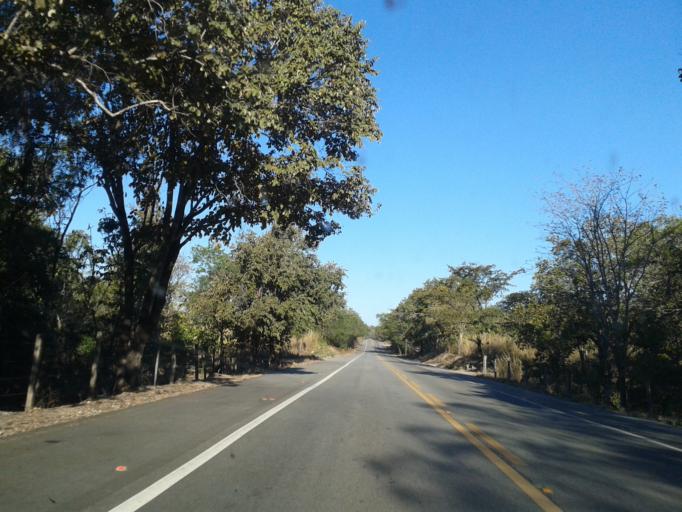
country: BR
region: Goias
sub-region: Itapuranga
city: Itapuranga
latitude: -15.4781
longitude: -50.3361
